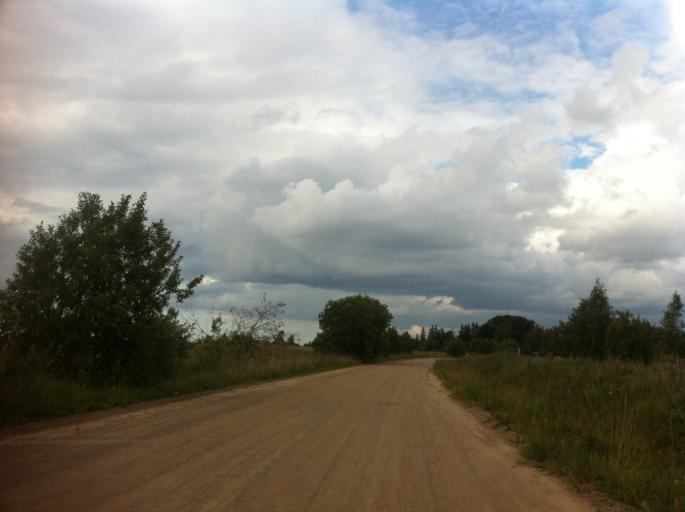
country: RU
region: Pskov
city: Izborsk
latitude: 57.8348
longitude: 27.9857
